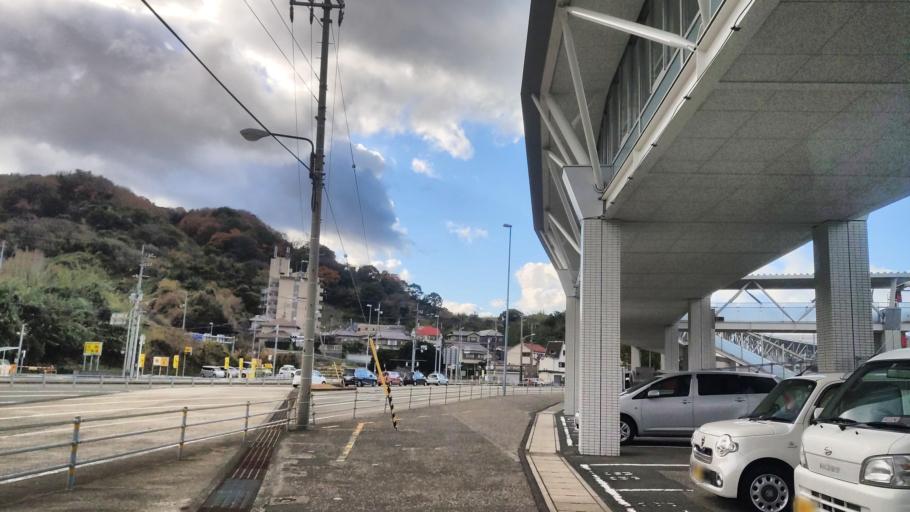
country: JP
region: Ehime
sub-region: Shikoku-chuo Shi
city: Matsuyama
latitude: 33.8899
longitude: 132.7057
